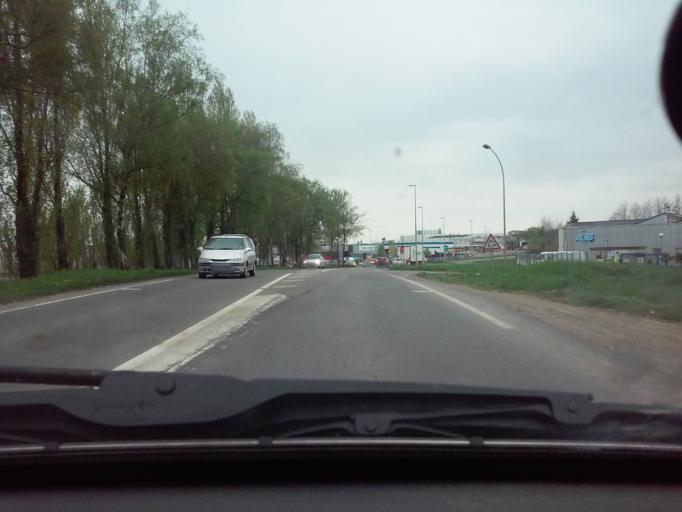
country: FR
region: Brittany
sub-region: Departement d'Ille-et-Vilaine
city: Beauce
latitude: 48.3378
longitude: -1.1761
